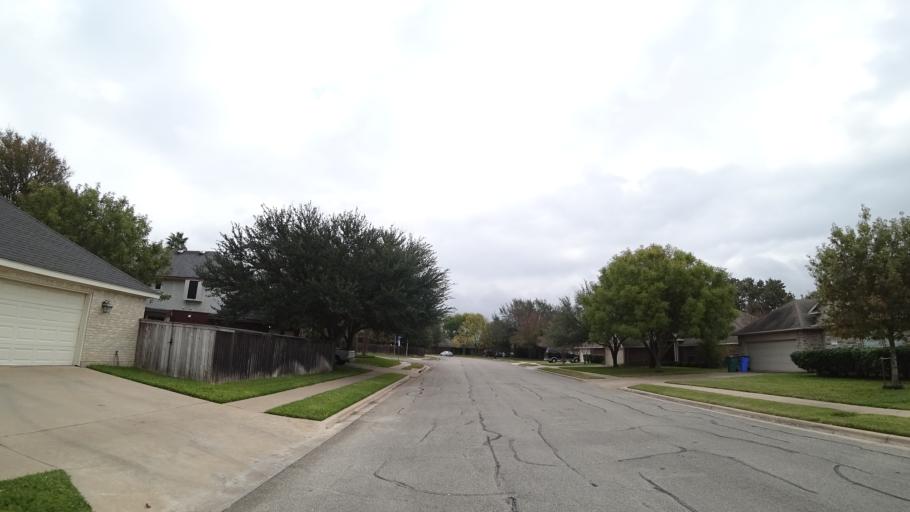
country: US
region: Texas
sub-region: Travis County
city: Pflugerville
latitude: 30.4464
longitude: -97.6110
